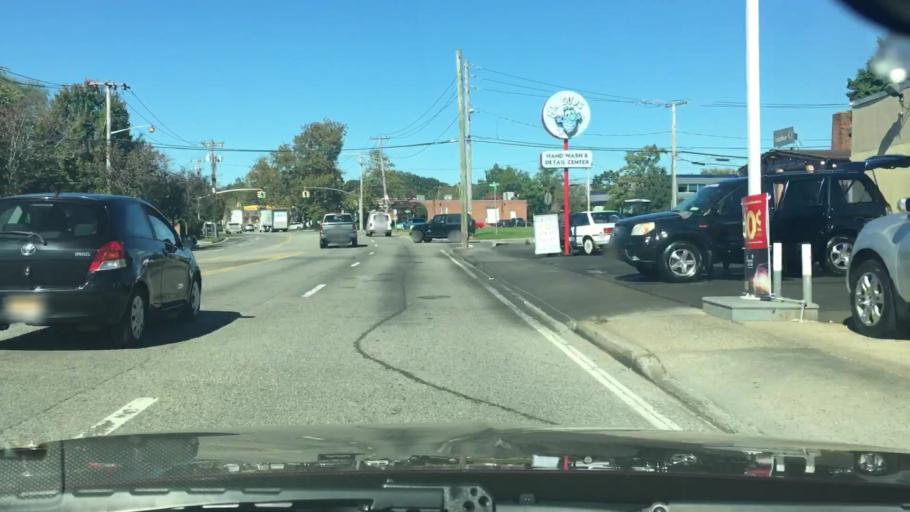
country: US
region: New York
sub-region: Nassau County
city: Port Washington North
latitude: 40.8390
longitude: -73.7038
